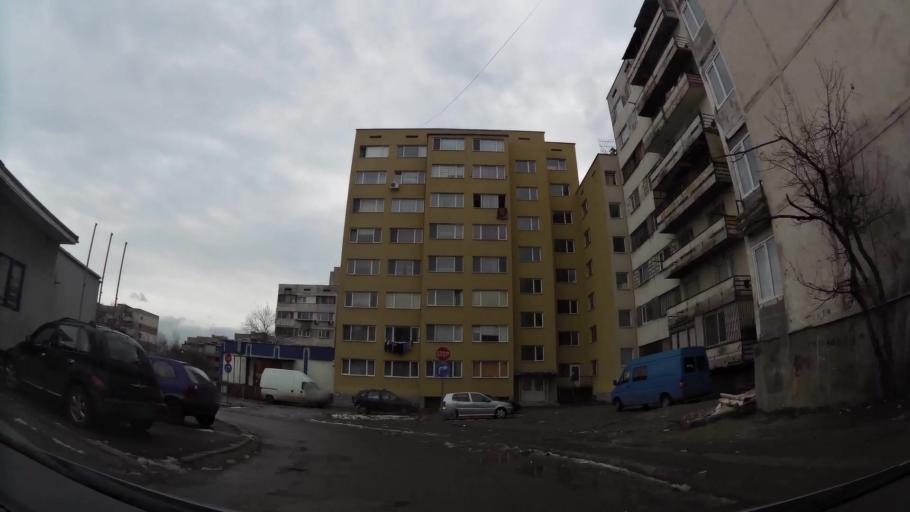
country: BG
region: Sofiya
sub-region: Obshtina Bozhurishte
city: Bozhurishte
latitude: 42.7292
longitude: 23.2491
